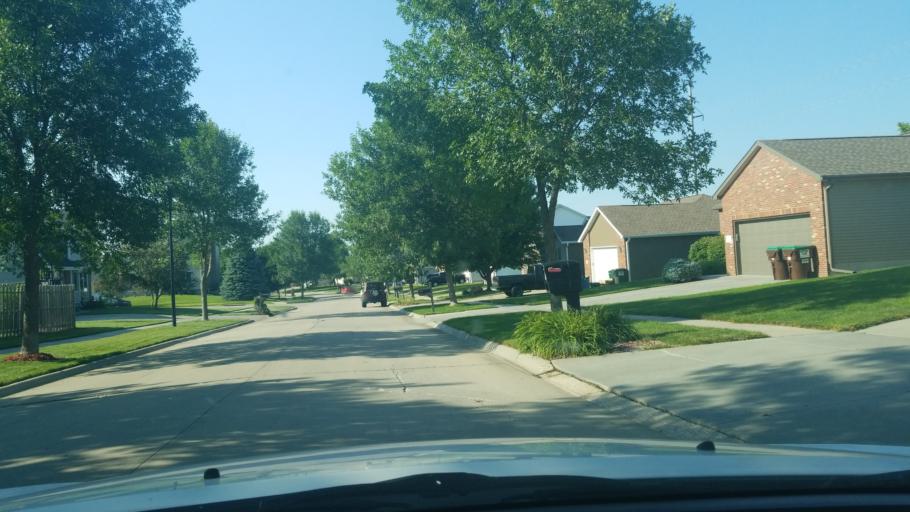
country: US
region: Nebraska
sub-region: Lancaster County
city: Lincoln
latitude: 40.7518
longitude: -96.6109
